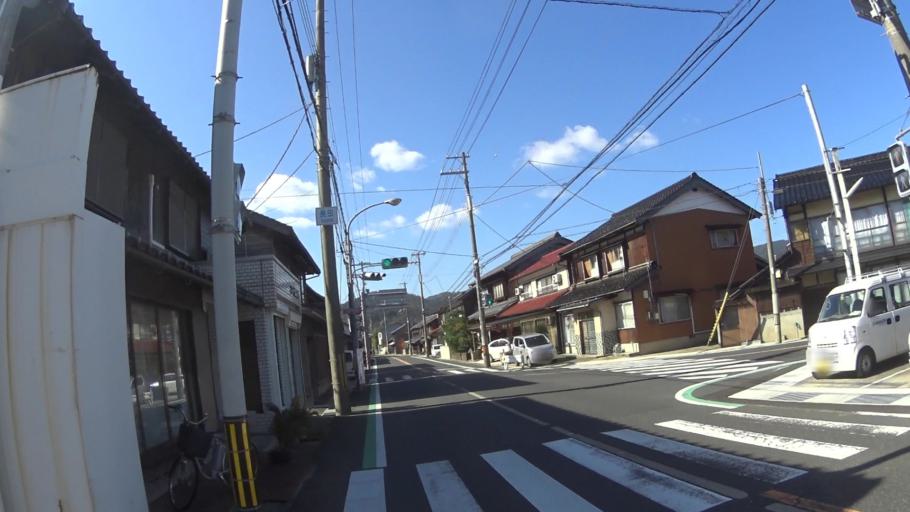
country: JP
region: Kyoto
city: Miyazu
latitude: 35.6798
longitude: 135.0306
